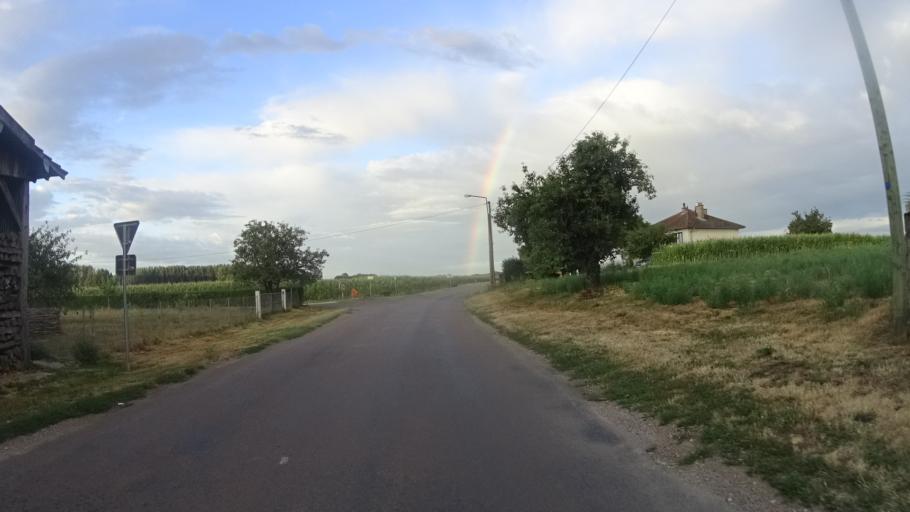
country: FR
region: Bourgogne
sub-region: Departement de la Cote-d'Or
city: Seurre
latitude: 46.9733
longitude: 5.0915
